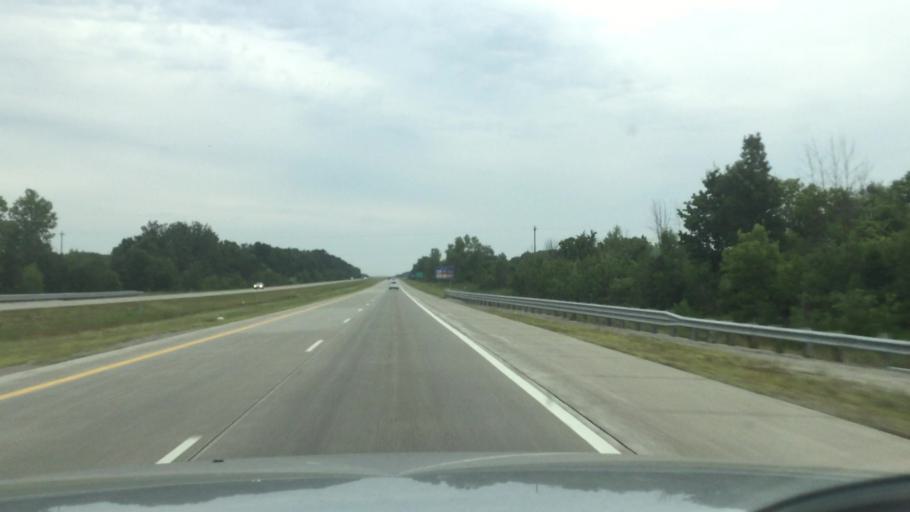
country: US
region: Michigan
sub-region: Genesee County
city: Grand Blanc
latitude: 42.9276
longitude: -83.6809
